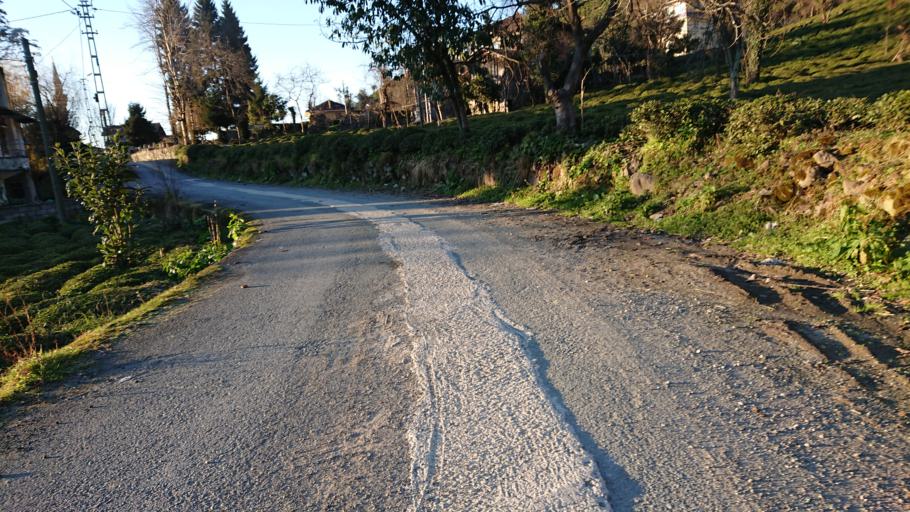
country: TR
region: Rize
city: Rize
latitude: 40.9820
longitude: 40.4952
